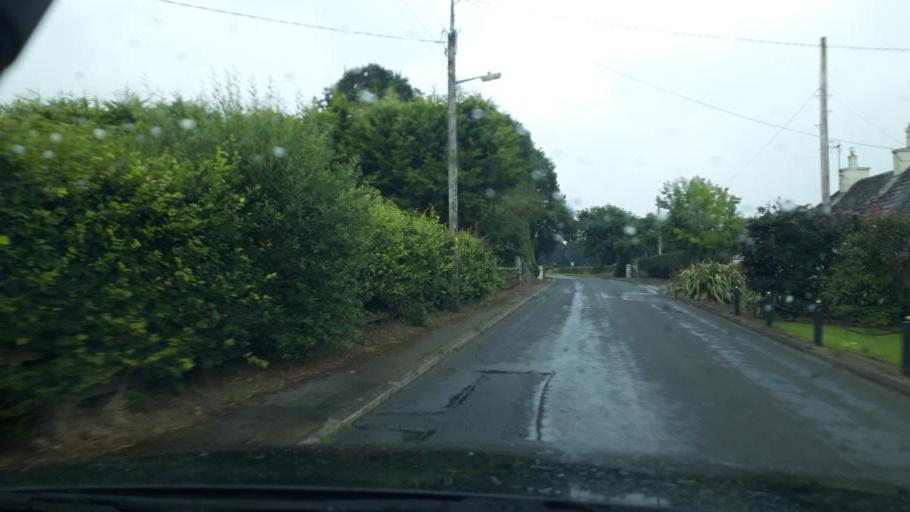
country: IE
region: Leinster
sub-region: Kilkenny
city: Callan
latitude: 52.6615
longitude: -7.4377
